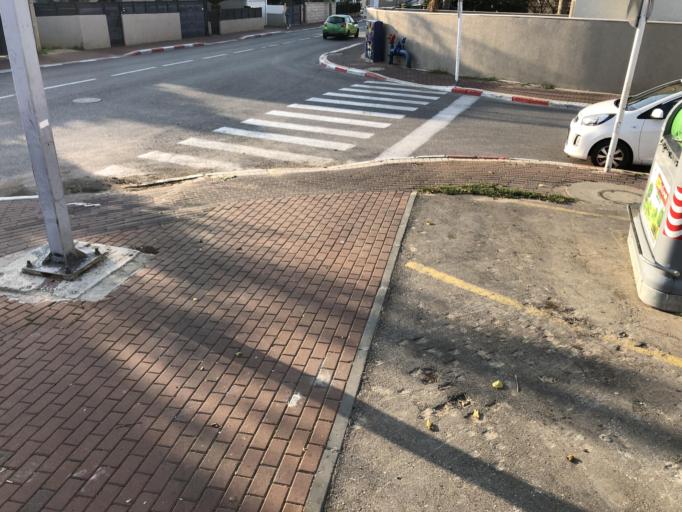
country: IL
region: Northern District
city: `Akko
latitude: 32.9267
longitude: 35.0883
